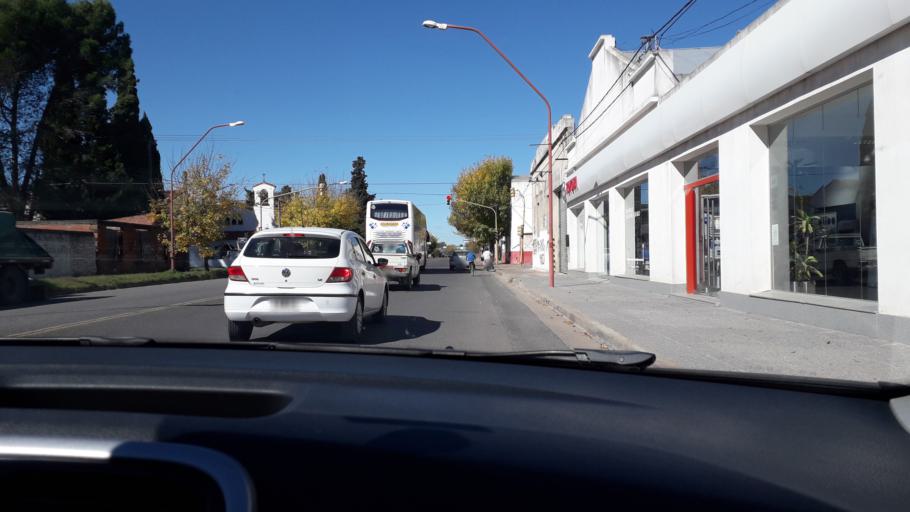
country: AR
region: Buenos Aires
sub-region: Partido de Azul
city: Azul
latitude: -36.7871
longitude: -59.8470
